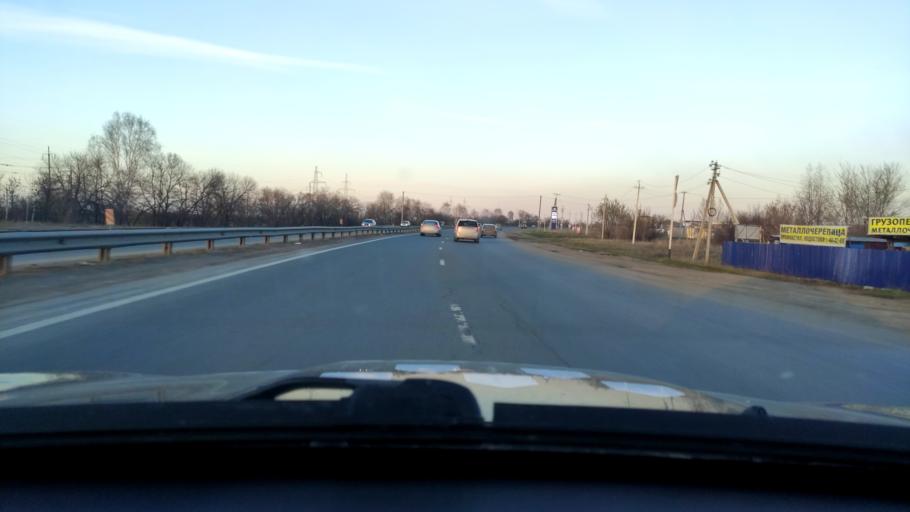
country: RU
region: Samara
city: Tol'yatti
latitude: 53.5793
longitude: 49.4065
